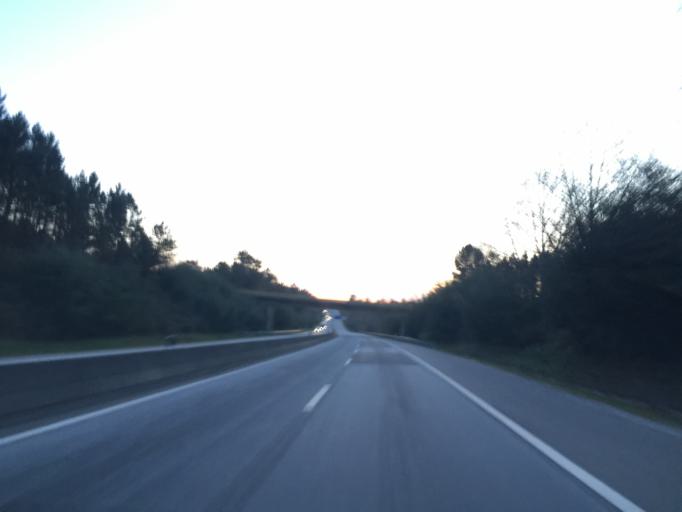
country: PT
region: Viseu
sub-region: Santa Comba Dao
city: Santa Comba Dao
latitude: 40.3970
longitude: -8.0959
